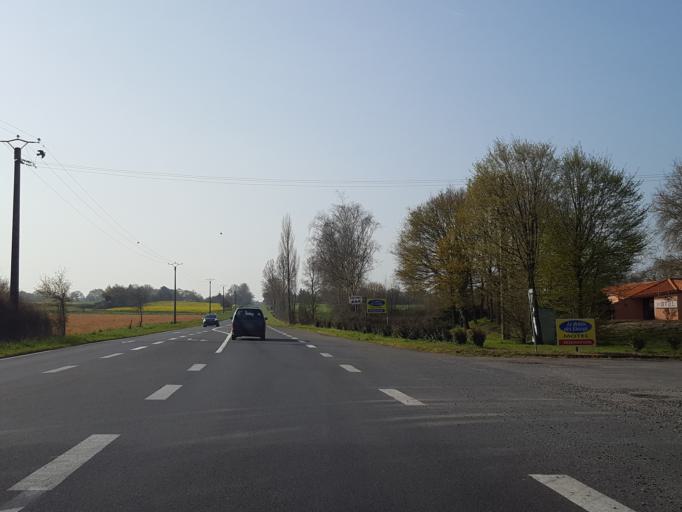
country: FR
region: Pays de la Loire
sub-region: Departement de la Vendee
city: Saint-Philbert-de-Bouaine
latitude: 46.9750
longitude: -1.5182
